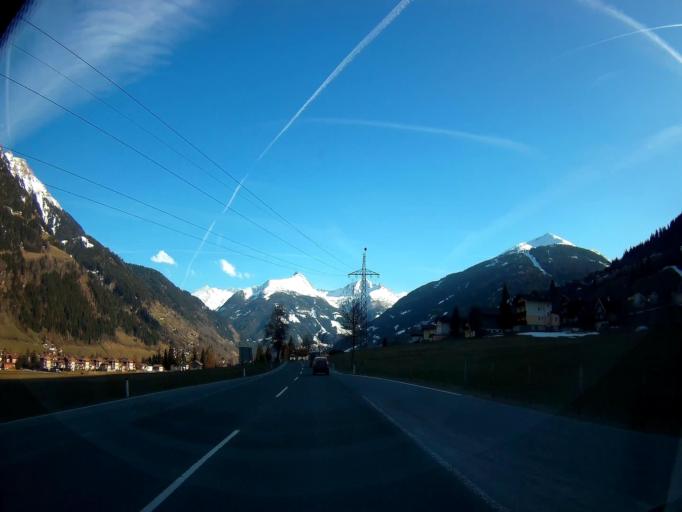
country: AT
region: Salzburg
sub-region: Politischer Bezirk Sankt Johann im Pongau
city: Bad Hofgastein
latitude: 47.1626
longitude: 13.1008
